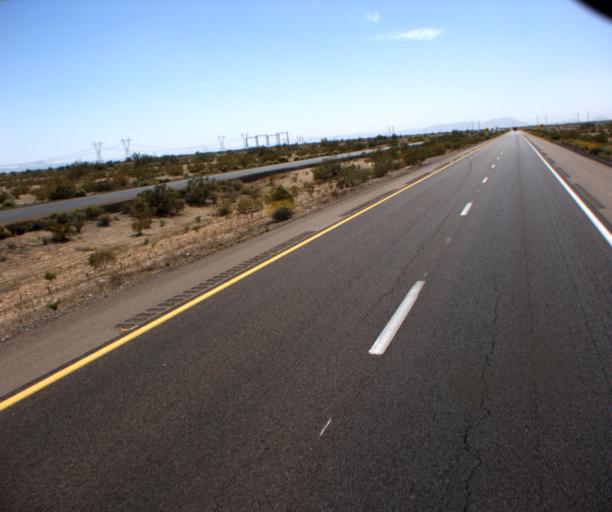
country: US
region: Arizona
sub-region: Maricopa County
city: Gila Bend
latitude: 32.9876
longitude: -112.6654
